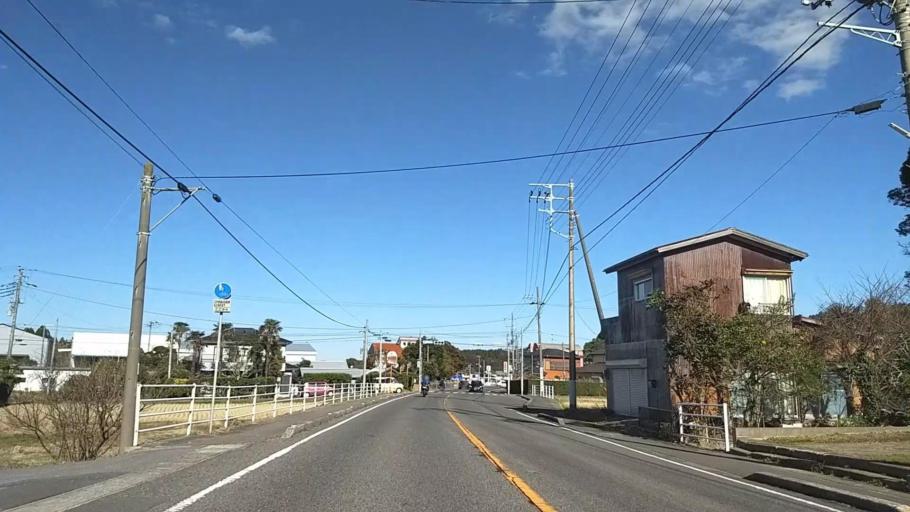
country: JP
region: Chiba
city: Ohara
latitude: 35.2187
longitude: 140.3790
